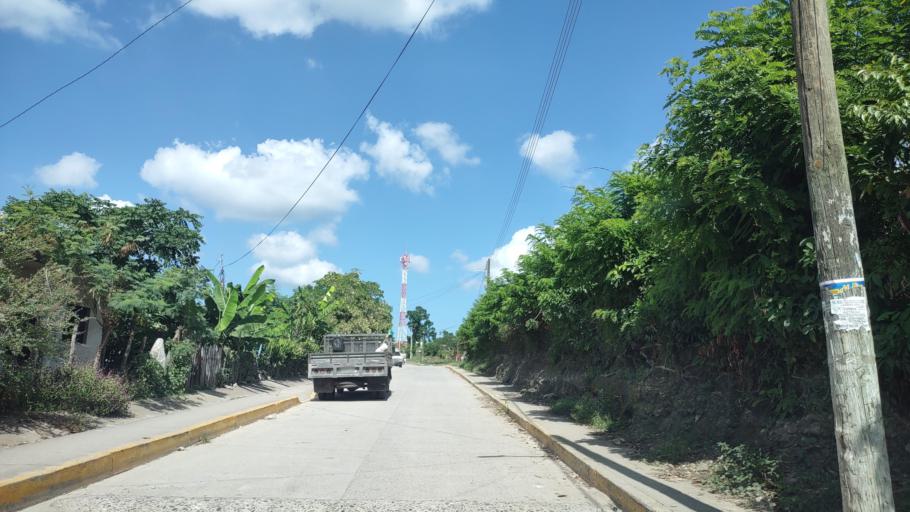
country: MM
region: Shan
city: Taunggyi
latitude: 20.5857
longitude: 97.3739
